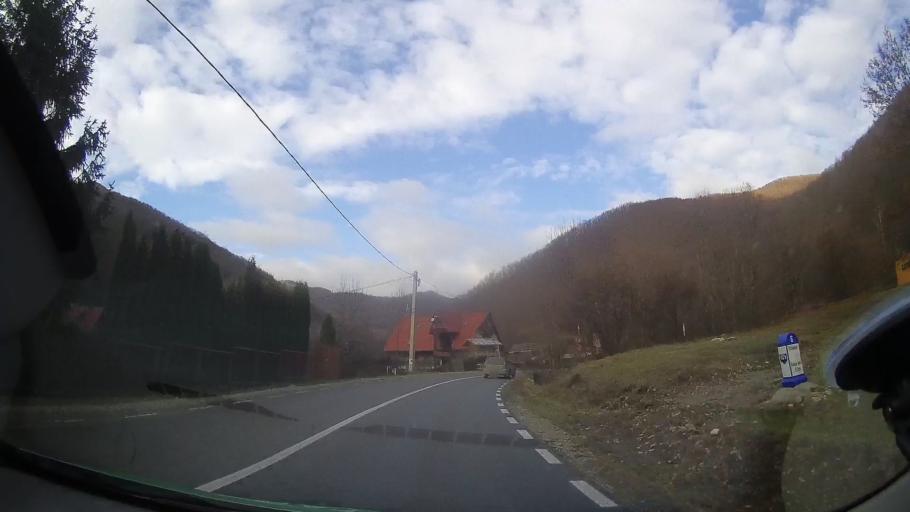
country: RO
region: Cluj
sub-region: Comuna Baisoara
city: Baisoara
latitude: 46.6106
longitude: 23.4131
